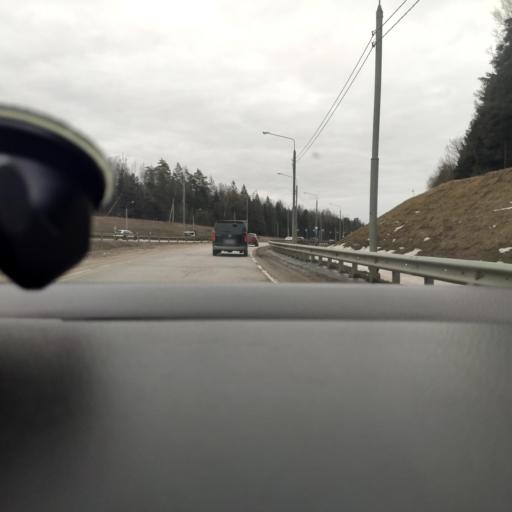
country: RU
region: Moskovskaya
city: Yershovo
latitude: 55.8216
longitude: 36.9261
